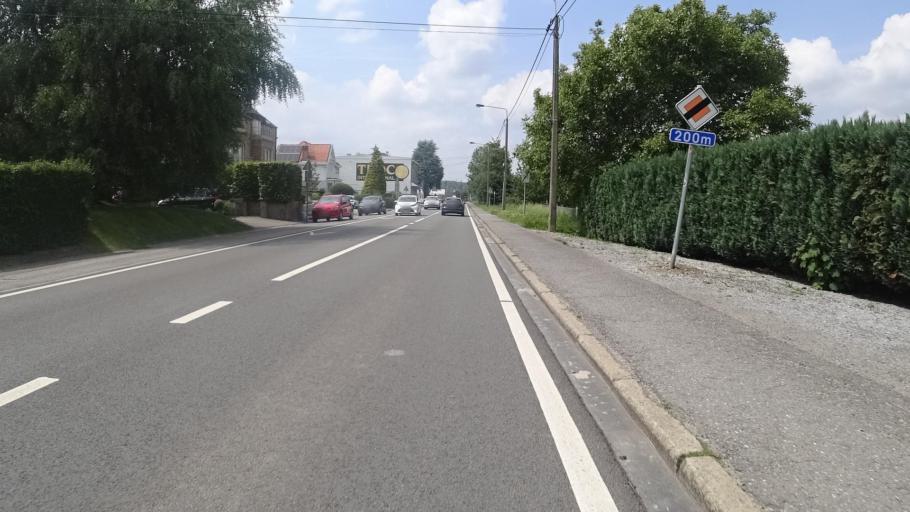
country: BE
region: Wallonia
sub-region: Province du Brabant Wallon
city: Wavre
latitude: 50.7091
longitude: 4.6193
